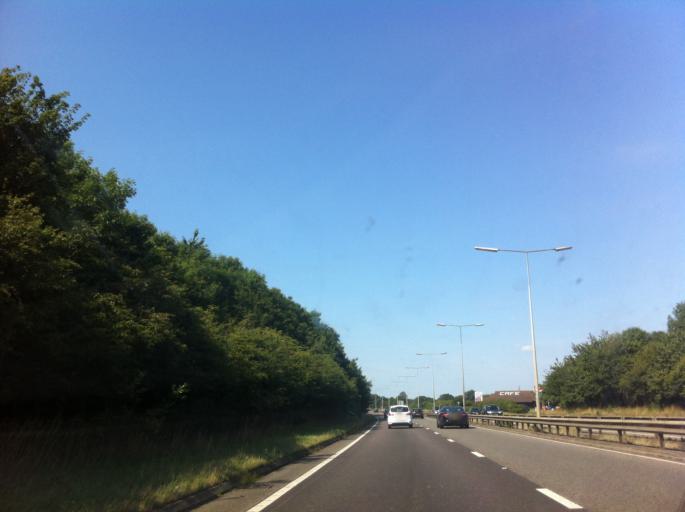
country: GB
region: England
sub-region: Northamptonshire
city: Earls Barton
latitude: 52.2554
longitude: -0.7876
